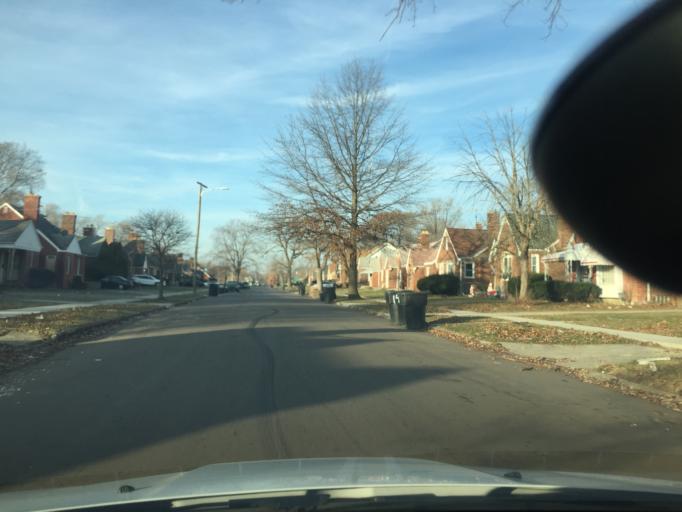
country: US
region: Michigan
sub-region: Macomb County
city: Eastpointe
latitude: 42.4417
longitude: -82.9691
